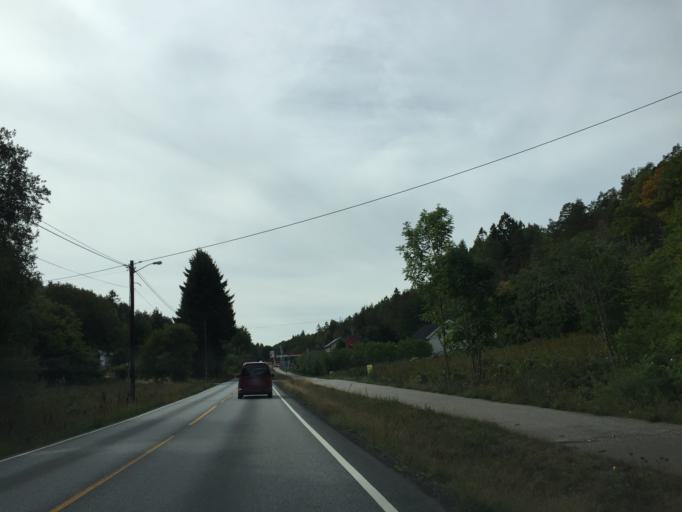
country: NO
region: Ostfold
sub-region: Fredrikstad
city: Fredrikstad
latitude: 59.1081
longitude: 10.9077
